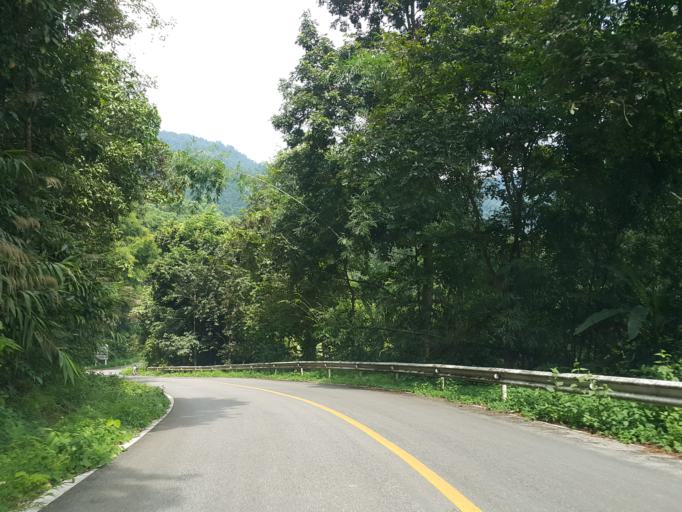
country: TH
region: Mae Hong Son
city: Mae Hong Son
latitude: 19.4883
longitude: 97.9578
